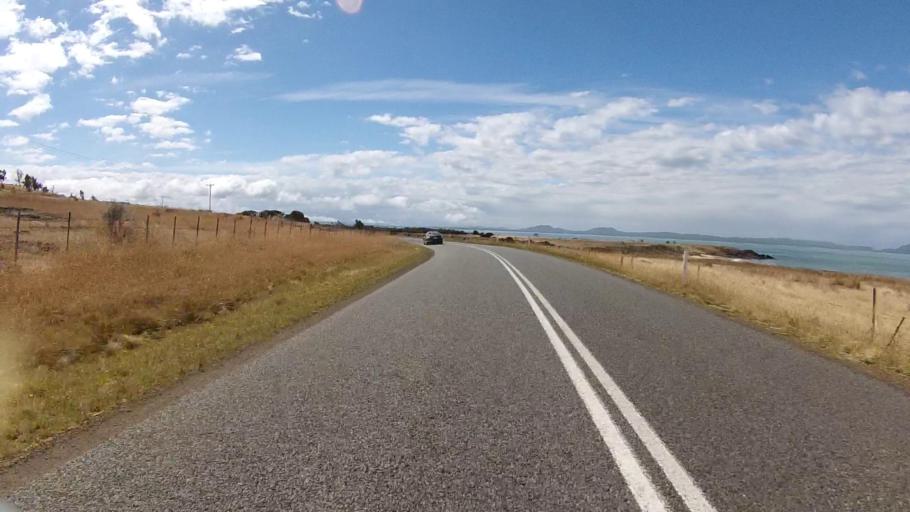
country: AU
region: Tasmania
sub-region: Sorell
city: Sorell
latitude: -42.1722
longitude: 148.0733
